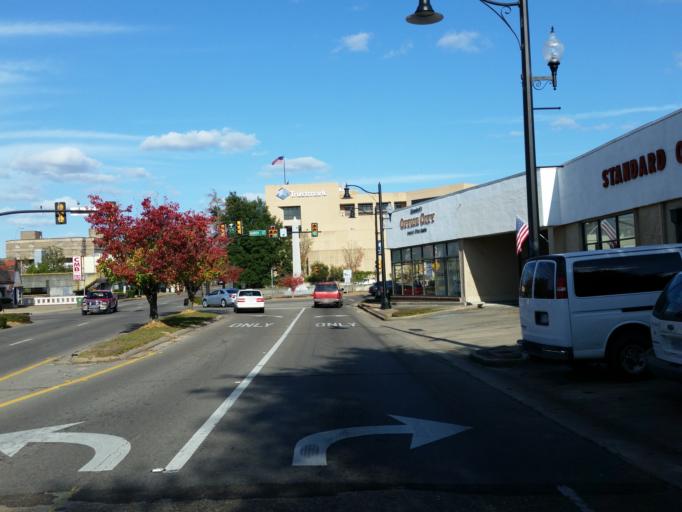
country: US
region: Mississippi
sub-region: Forrest County
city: Hattiesburg
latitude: 31.3243
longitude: -89.2932
